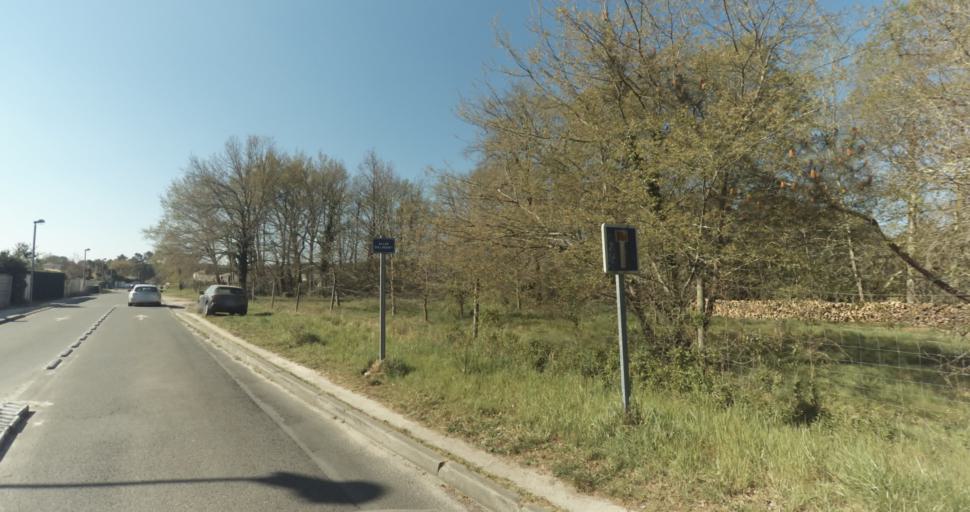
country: FR
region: Aquitaine
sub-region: Departement de la Gironde
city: Martignas-sur-Jalle
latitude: 44.8047
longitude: -0.7952
